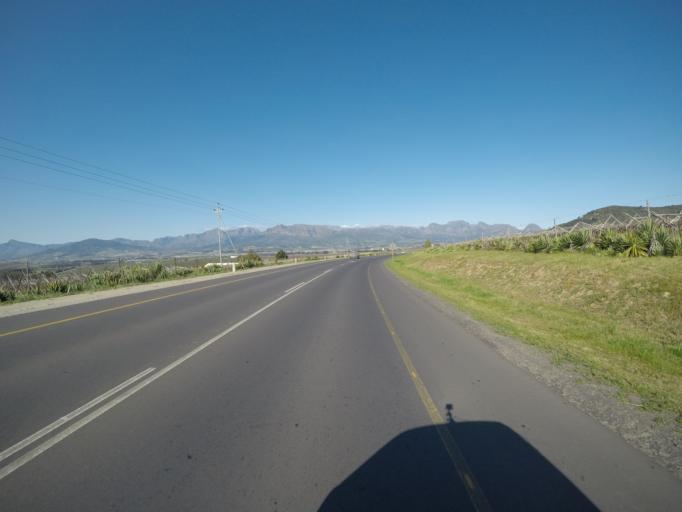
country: ZA
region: Western Cape
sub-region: Cape Winelands District Municipality
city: Noorder-Paarl
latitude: -33.6702
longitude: 18.9268
